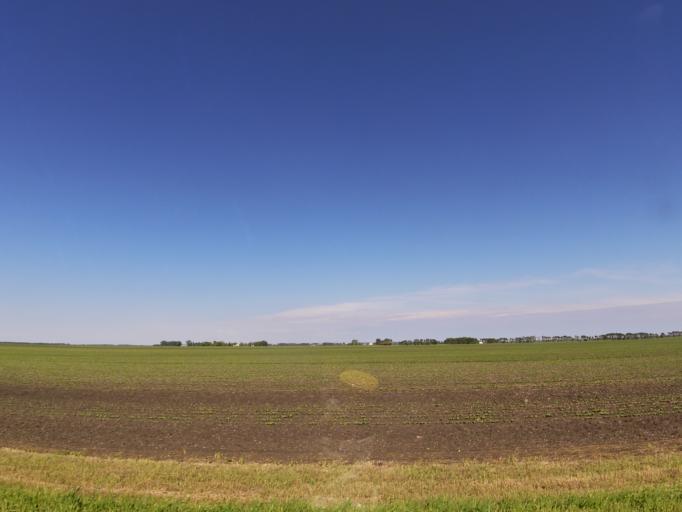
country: US
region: North Dakota
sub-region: Walsh County
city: Grafton
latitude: 48.3465
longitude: -97.2558
